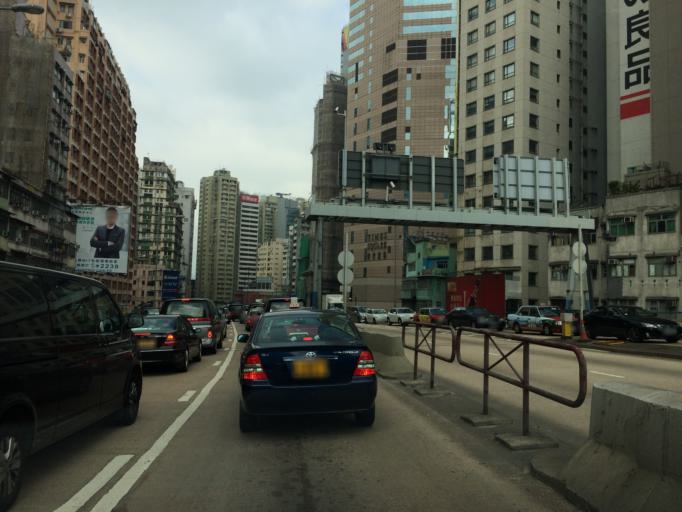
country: HK
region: Wanchai
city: Wan Chai
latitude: 22.2769
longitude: 114.1811
